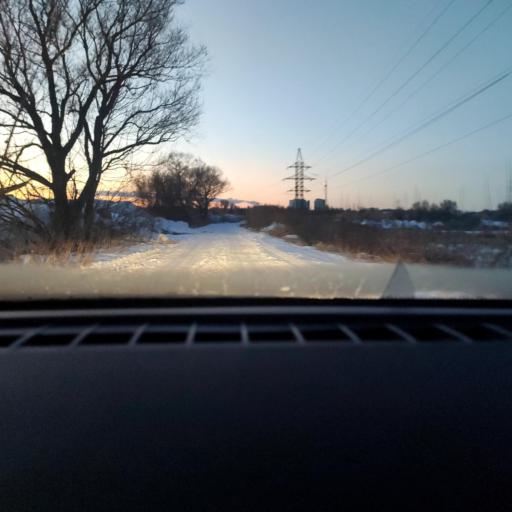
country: RU
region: Voronezj
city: Voronezh
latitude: 51.6209
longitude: 39.2200
